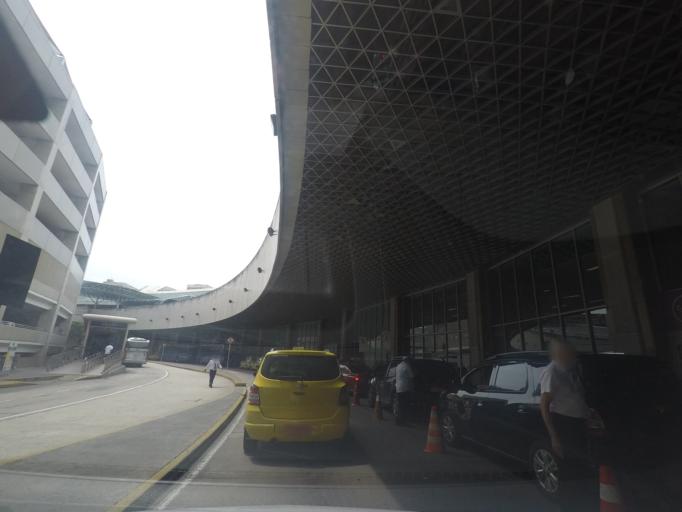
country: BR
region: Rio de Janeiro
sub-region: Duque De Caxias
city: Duque de Caxias
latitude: -22.8141
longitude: -43.2467
